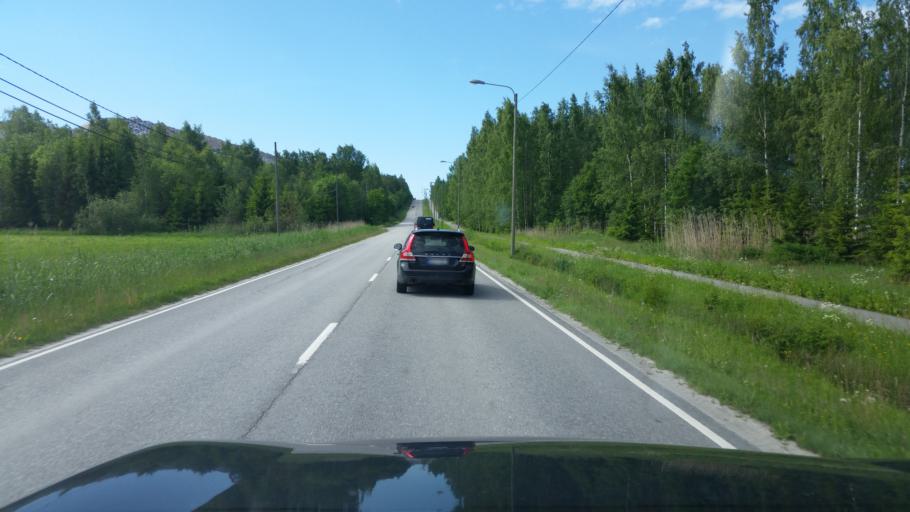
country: FI
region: Varsinais-Suomi
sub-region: Aboland-Turunmaa
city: Laensi-Turunmaa
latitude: 60.2955
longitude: 22.2690
